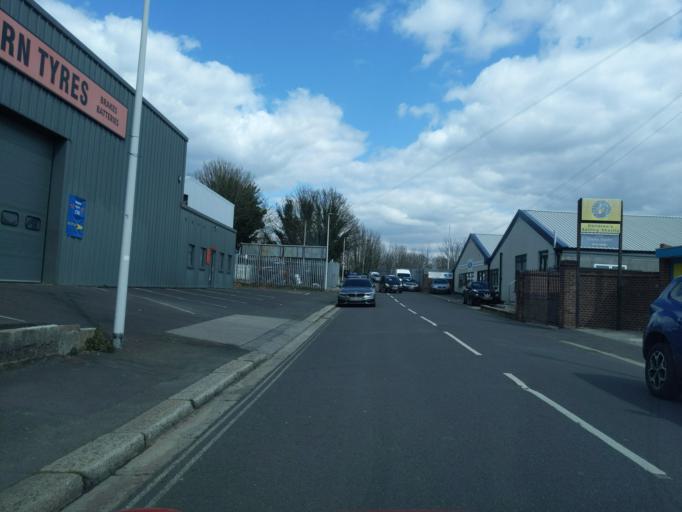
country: GB
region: England
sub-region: Cornwall
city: Millbrook
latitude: 50.3686
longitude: -4.1662
